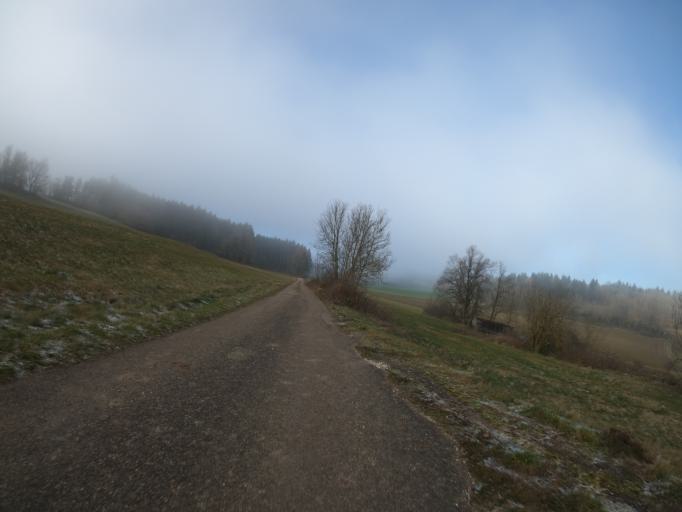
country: DE
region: Baden-Wuerttemberg
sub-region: Regierungsbezirk Stuttgart
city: Deggingen
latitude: 48.5923
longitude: 9.7506
